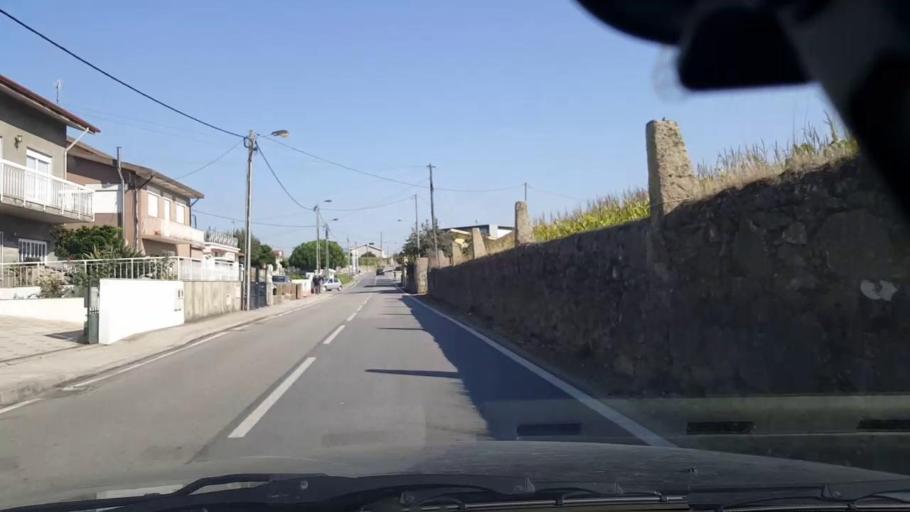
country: PT
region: Porto
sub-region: Maia
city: Gemunde
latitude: 41.2994
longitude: -8.6798
